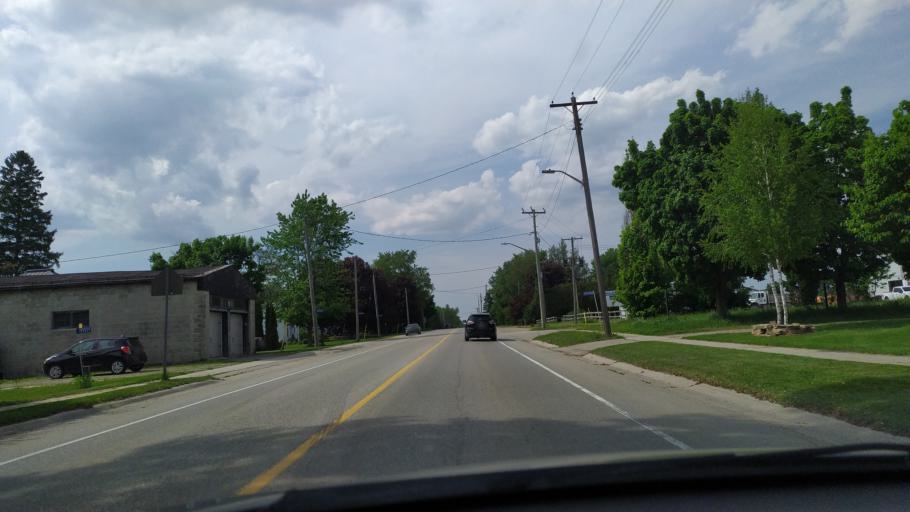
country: CA
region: Ontario
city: Dorchester
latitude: 43.1396
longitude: -81.0305
